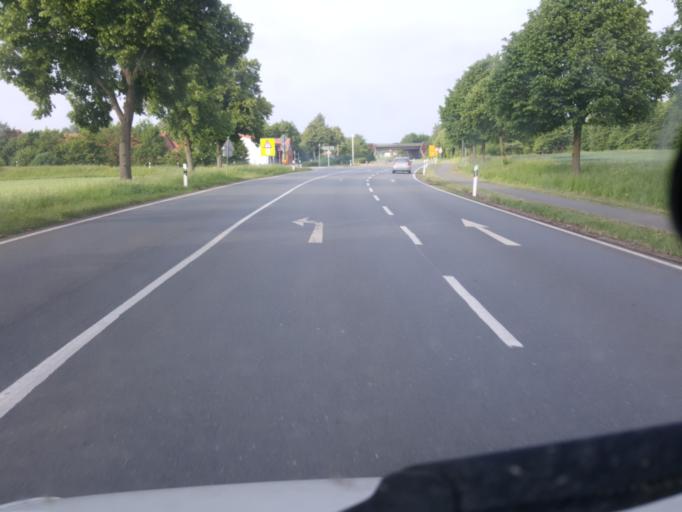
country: DE
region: Lower Saxony
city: Marklohe
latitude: 52.6510
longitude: 9.1495
